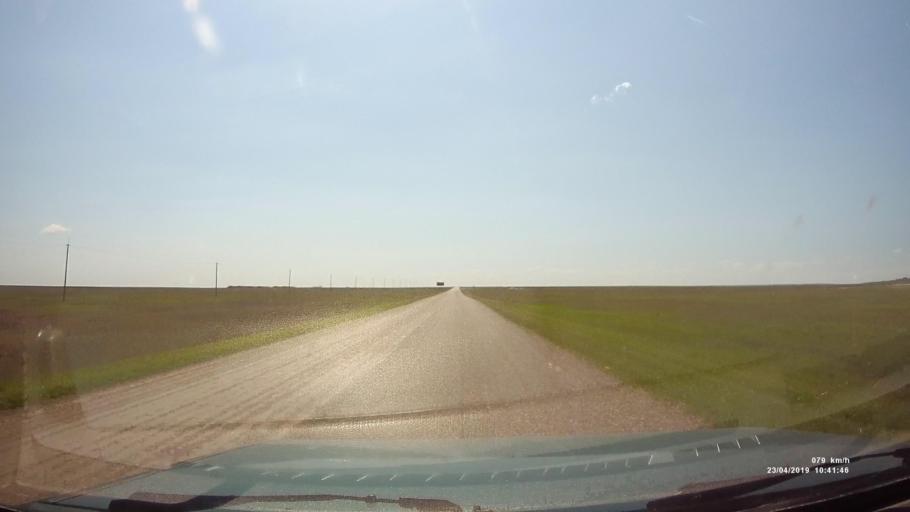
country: RU
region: Kalmykiya
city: Yashalta
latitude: 46.4904
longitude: 42.6390
